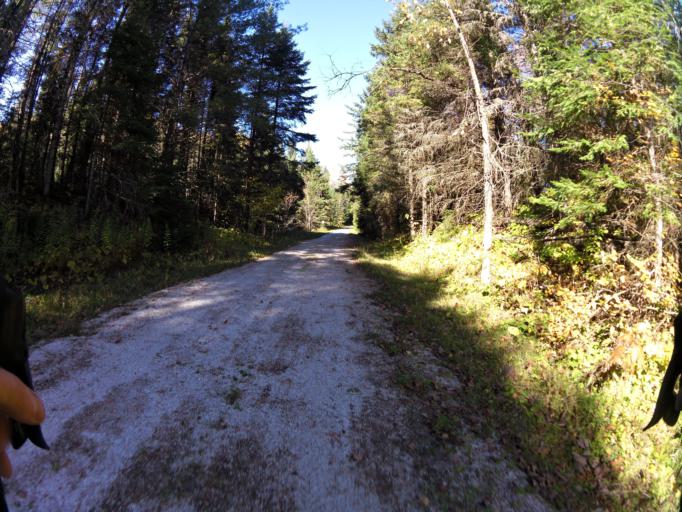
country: CA
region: Quebec
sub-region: Outaouais
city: Wakefield
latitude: 45.8524
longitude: -75.9915
